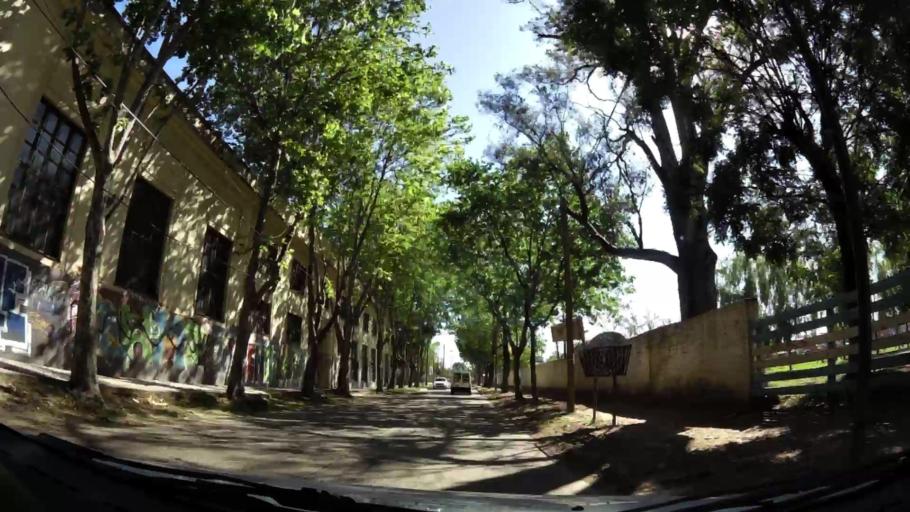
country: AR
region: Buenos Aires
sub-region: Partido de San Isidro
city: San Isidro
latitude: -34.4711
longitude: -58.5346
